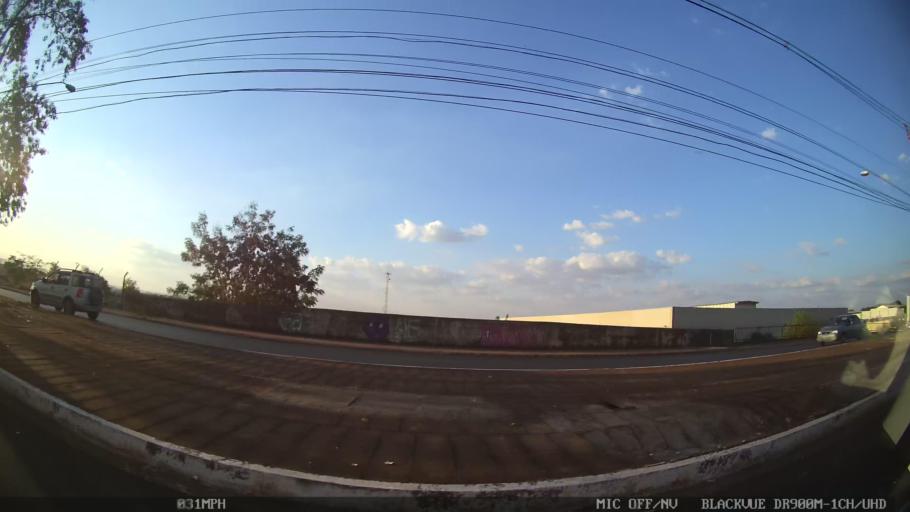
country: BR
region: Sao Paulo
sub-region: Ribeirao Preto
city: Ribeirao Preto
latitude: -21.1387
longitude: -47.7933
